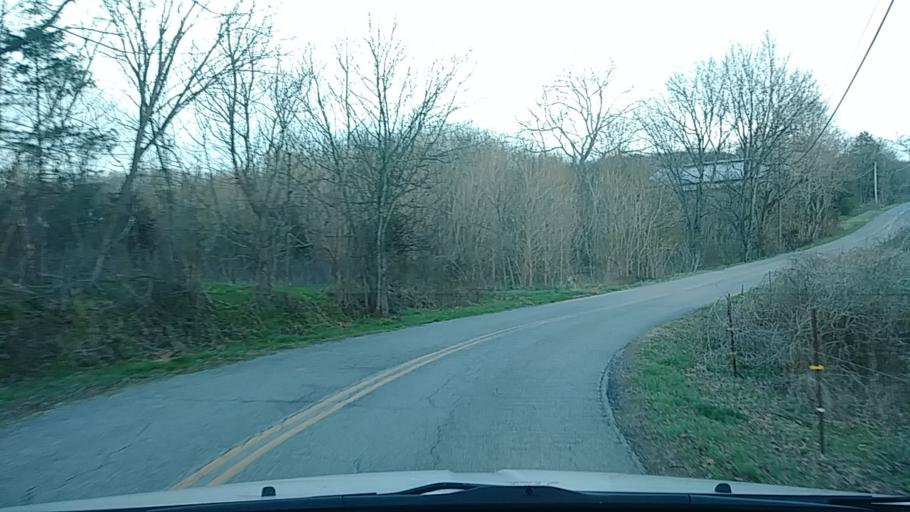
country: US
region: Tennessee
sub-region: Greene County
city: Mosheim
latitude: 36.1177
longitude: -82.9360
